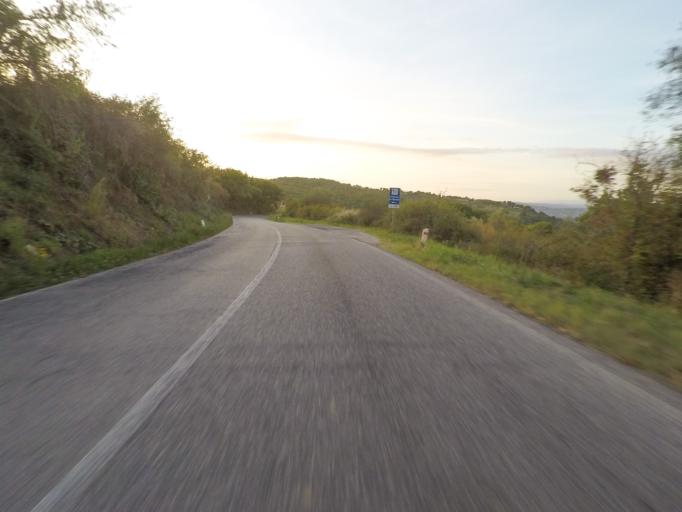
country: IT
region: Tuscany
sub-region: Provincia di Siena
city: Torrita di Siena
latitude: 43.1471
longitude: 11.7385
